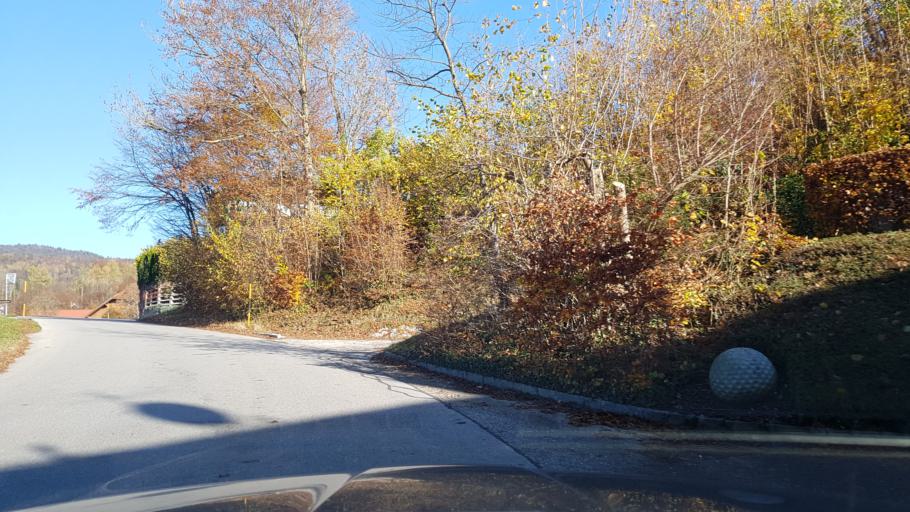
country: AT
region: Salzburg
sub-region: Politischer Bezirk Hallein
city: Puch bei Hallein
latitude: 47.7257
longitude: 13.1024
